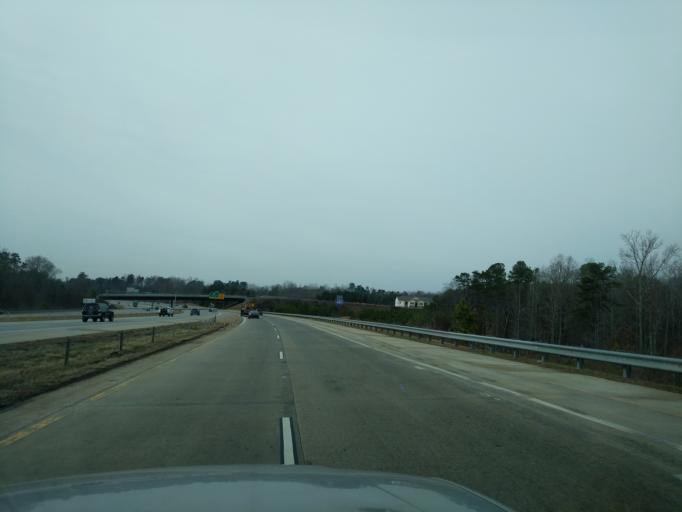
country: US
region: North Carolina
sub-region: Mecklenburg County
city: Huntersville
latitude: 35.3630
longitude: -80.8500
